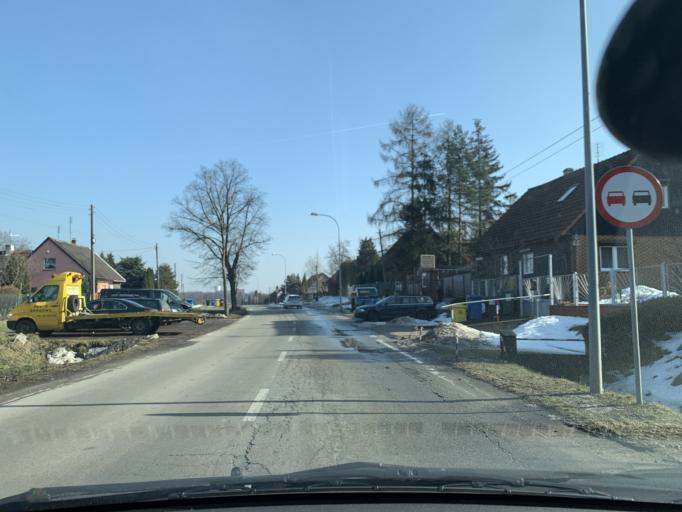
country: PL
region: Silesian Voivodeship
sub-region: Piekary Slaskie
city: Piekary Slaskie
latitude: 50.3614
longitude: 18.9067
